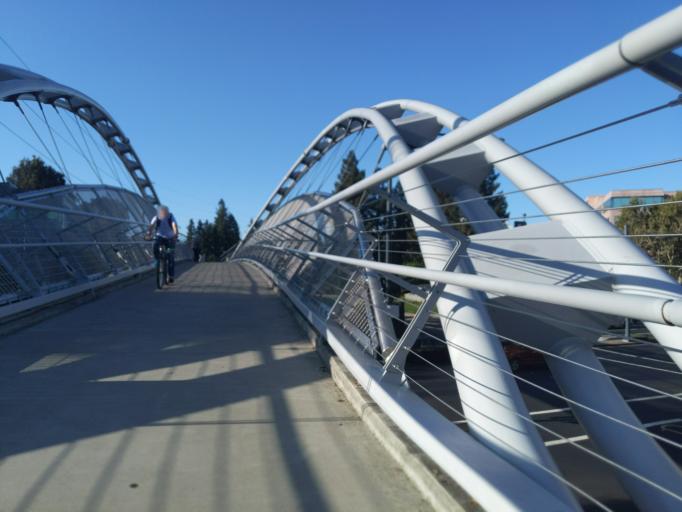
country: US
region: California
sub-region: Contra Costa County
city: Waldon
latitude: 37.9269
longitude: -122.0546
